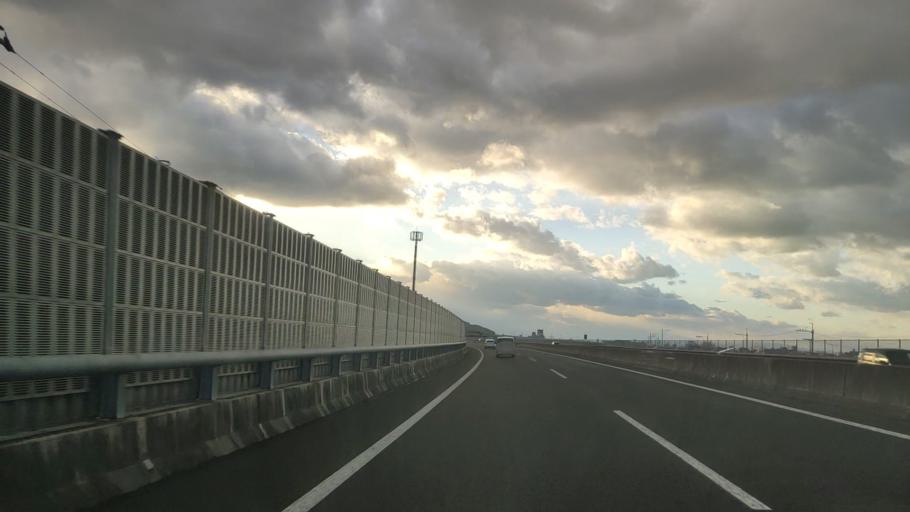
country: JP
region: Ehime
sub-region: Shikoku-chuo Shi
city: Matsuyama
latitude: 33.7888
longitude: 132.8236
